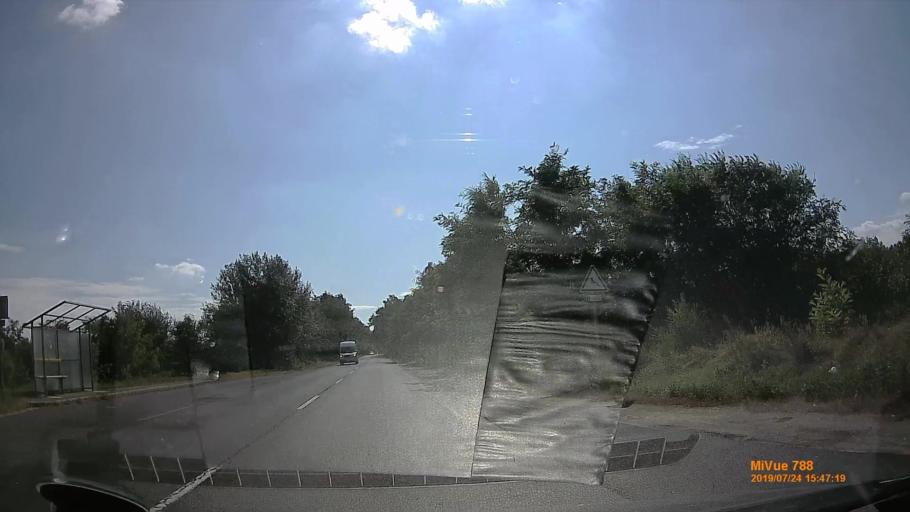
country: HU
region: Szabolcs-Szatmar-Bereg
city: Nyirmada
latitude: 48.0785
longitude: 22.2524
